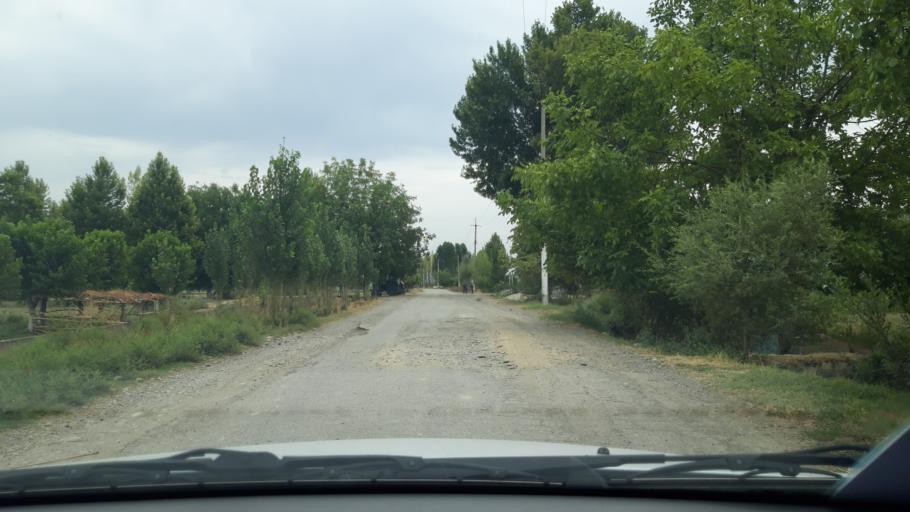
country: UZ
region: Namangan
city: Uychi
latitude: 41.0191
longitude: 71.9176
